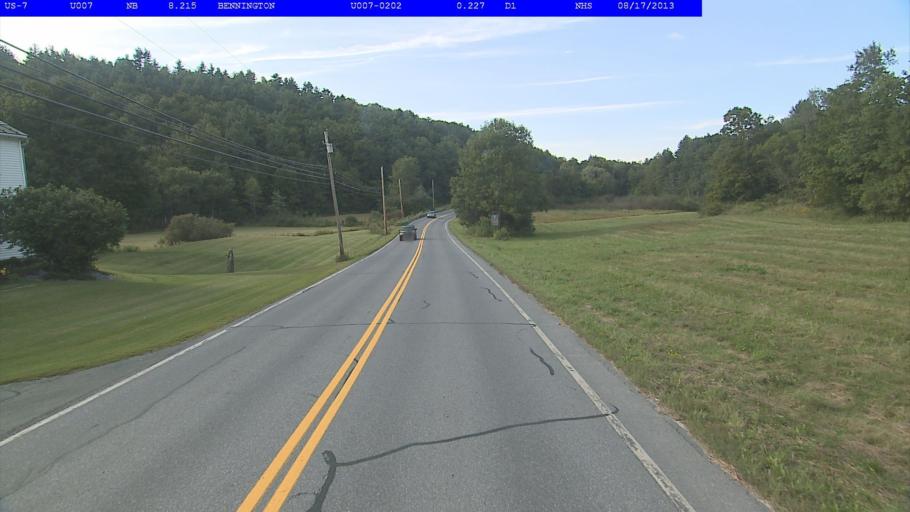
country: US
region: Vermont
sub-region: Bennington County
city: Bennington
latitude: 42.8408
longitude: -73.1999
